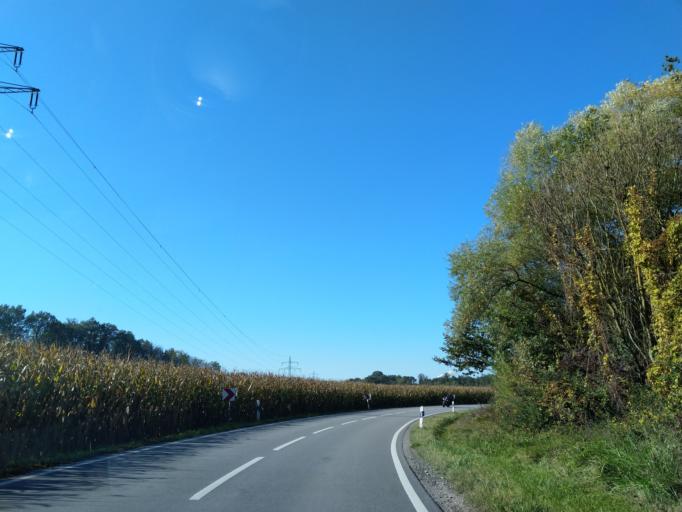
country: DE
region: Bavaria
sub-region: Lower Bavaria
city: Deggendorf
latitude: 48.8043
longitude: 12.9346
